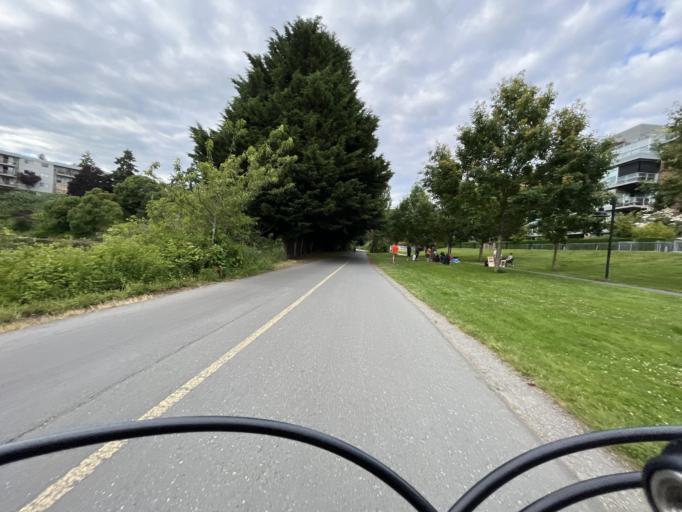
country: CA
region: British Columbia
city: Victoria
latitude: 48.4417
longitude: -123.3804
